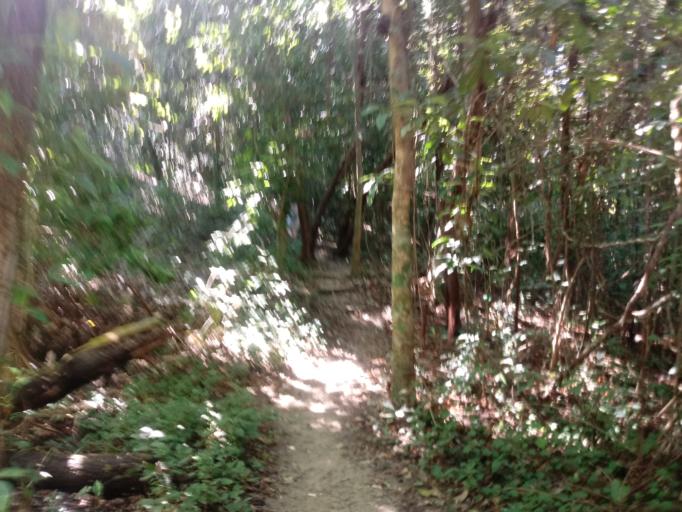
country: CR
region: Puntarenas
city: Paquera
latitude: 9.5864
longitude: -85.0971
